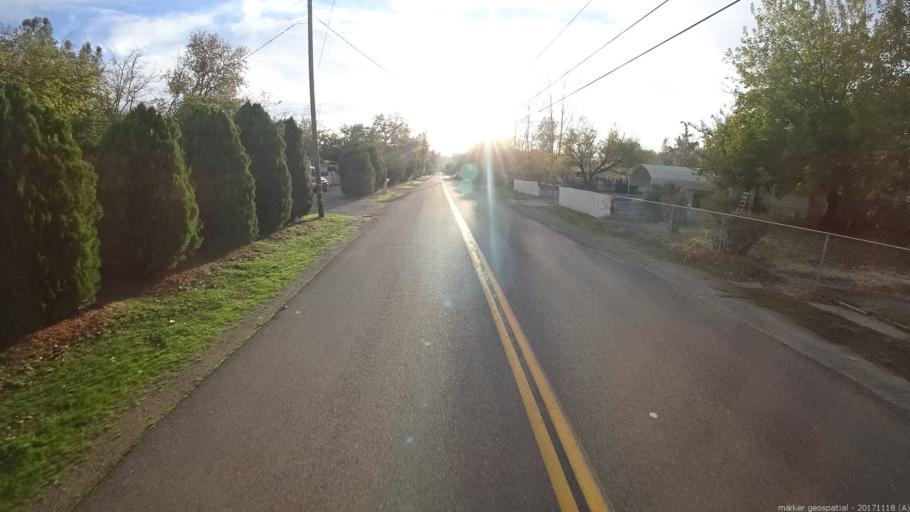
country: US
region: California
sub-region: Shasta County
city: Anderson
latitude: 40.4618
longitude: -122.3318
